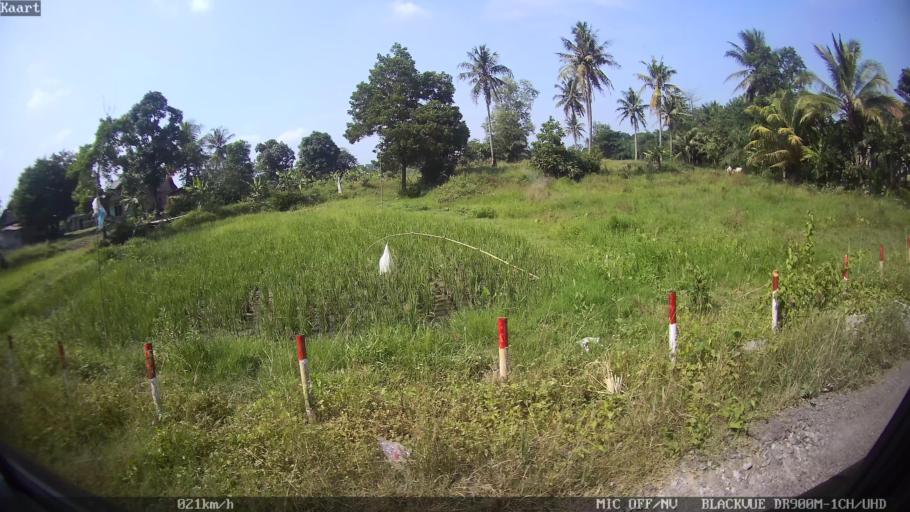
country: ID
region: Lampung
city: Natar
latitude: -5.2564
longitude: 105.2109
